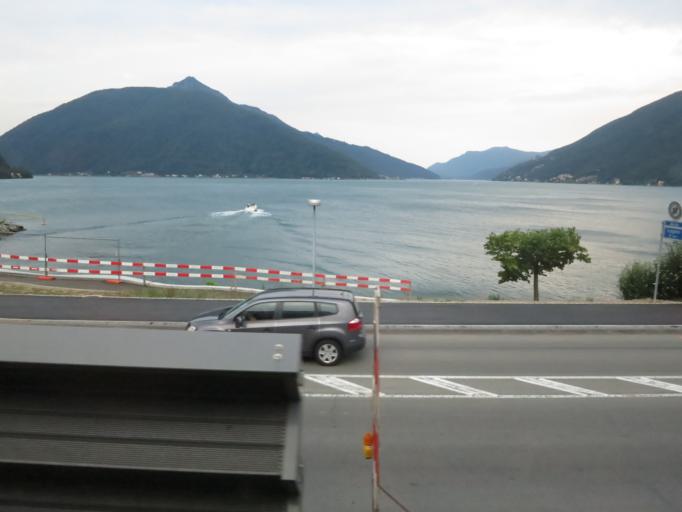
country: CH
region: Ticino
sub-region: Lugano District
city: Melide
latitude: 45.9528
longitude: 8.9634
